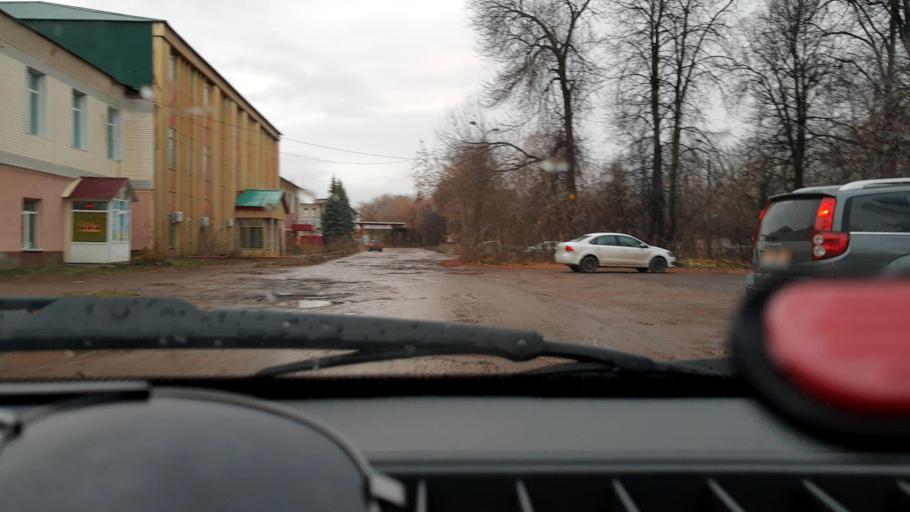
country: RU
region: Bashkortostan
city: Ufa
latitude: 54.7982
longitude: 56.0945
